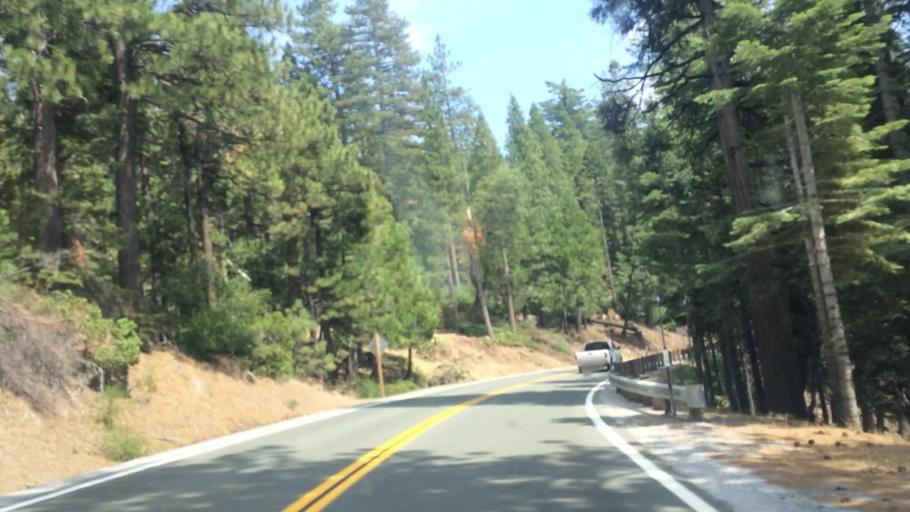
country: US
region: California
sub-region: Amador County
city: Pioneer
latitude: 38.5401
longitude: -120.3871
